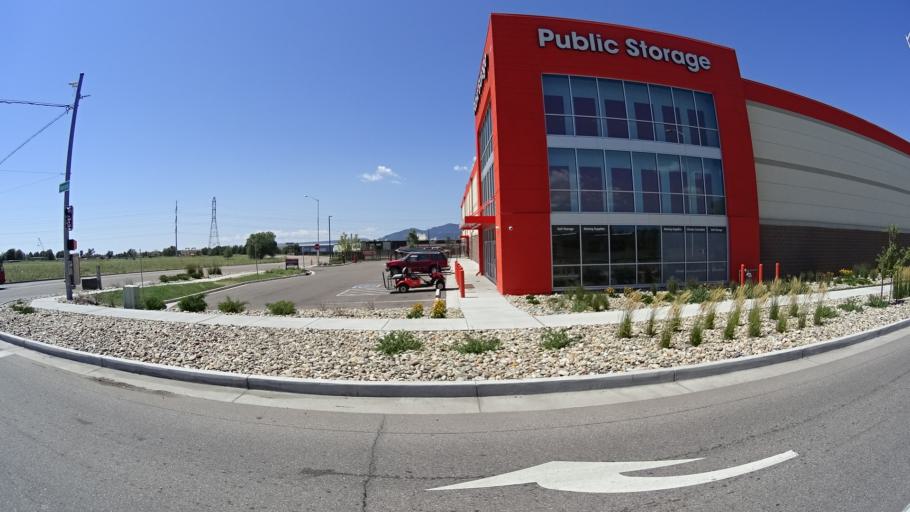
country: US
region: Colorado
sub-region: El Paso County
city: Stratmoor
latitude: 38.7909
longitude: -104.7632
